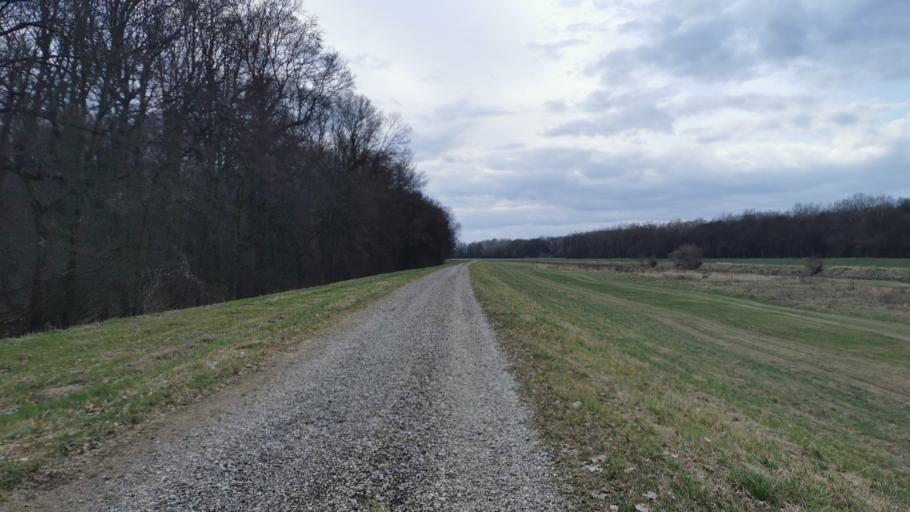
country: CZ
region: South Moravian
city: Hodonin
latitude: 48.8339
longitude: 17.1201
